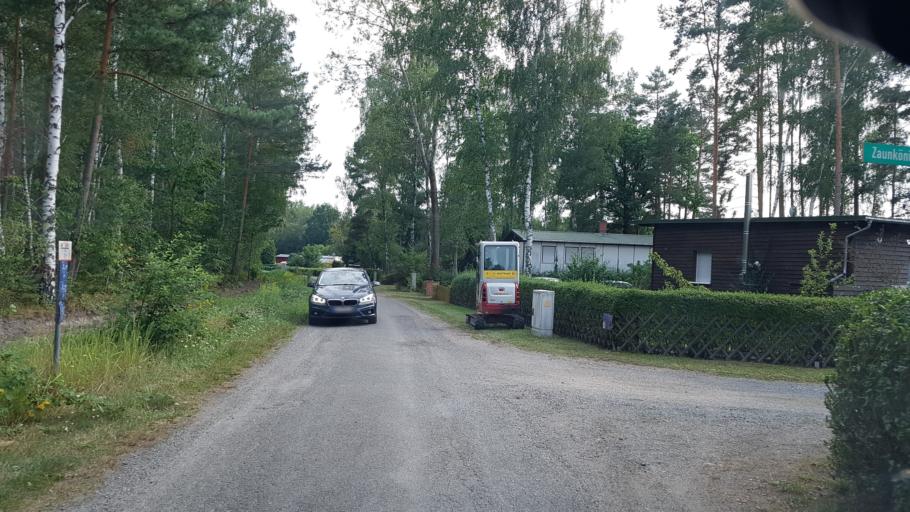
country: DE
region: Brandenburg
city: Plessa
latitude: 51.5148
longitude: 13.6692
